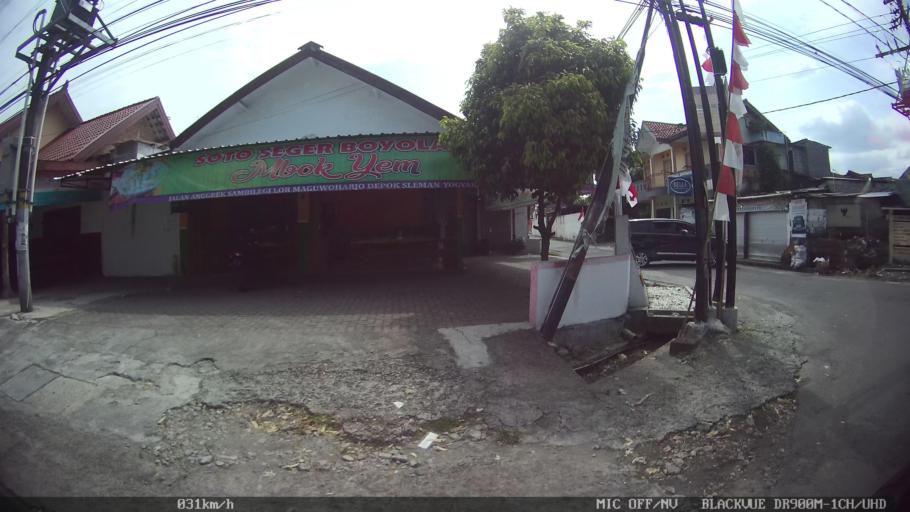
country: ID
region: Daerah Istimewa Yogyakarta
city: Depok
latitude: -7.7762
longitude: 110.4354
